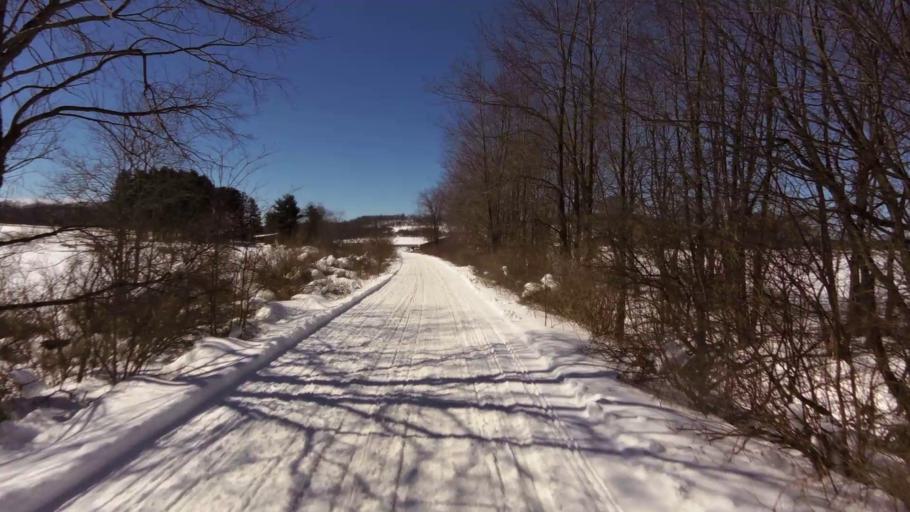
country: US
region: New York
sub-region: Cattaraugus County
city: Delevan
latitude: 42.4399
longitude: -78.4253
